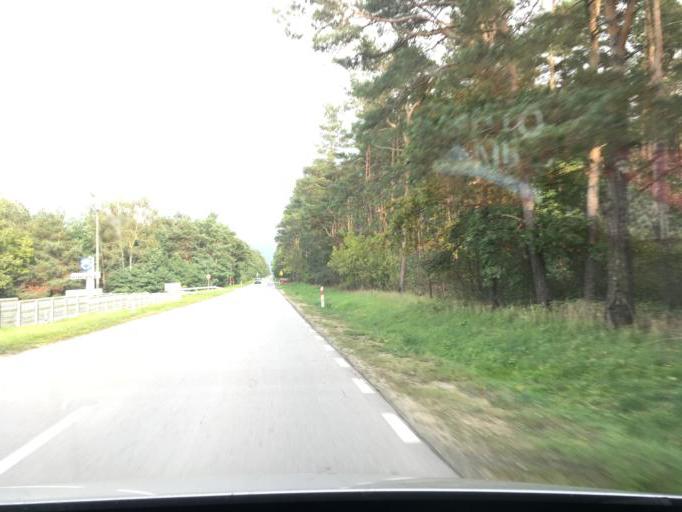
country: PL
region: Swietokrzyskie
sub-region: Powiat pinczowski
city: Michalow
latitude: 50.5017
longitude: 20.4834
